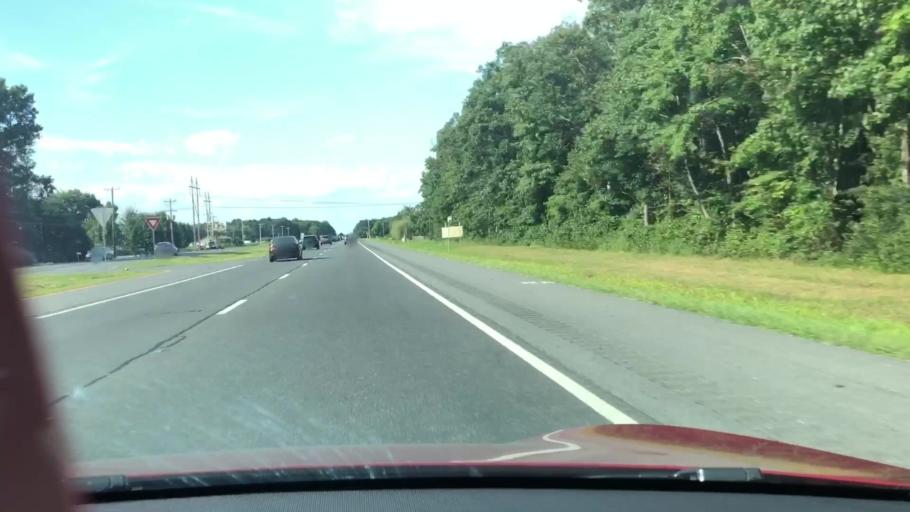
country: US
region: Delaware
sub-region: Kent County
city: Harrington
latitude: 38.8900
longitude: -75.5720
